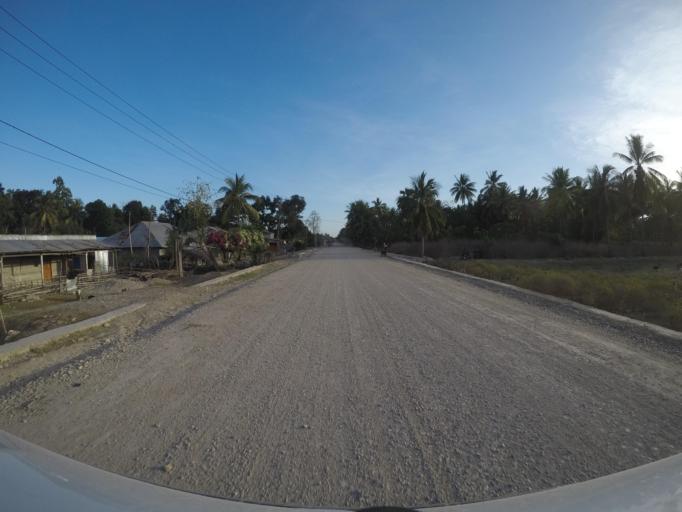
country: TL
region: Viqueque
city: Viqueque
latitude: -8.8507
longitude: 126.5126
